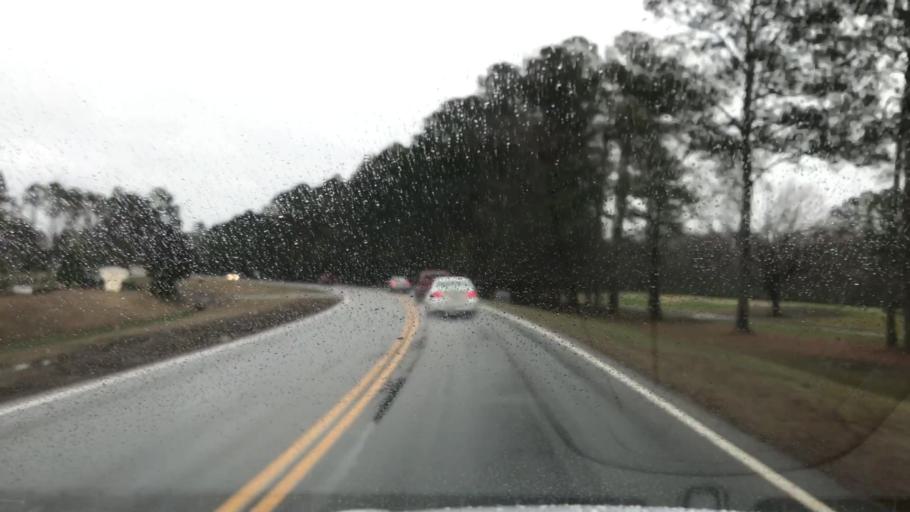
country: US
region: South Carolina
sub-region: Horry County
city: Forestbrook
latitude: 33.7282
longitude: -78.9121
